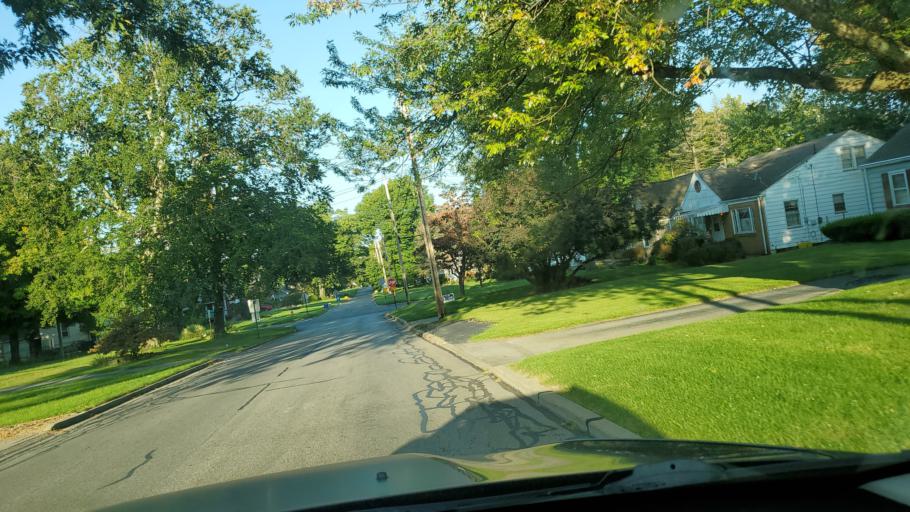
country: US
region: Ohio
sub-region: Mahoning County
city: Boardman
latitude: 41.0426
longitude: -80.6523
